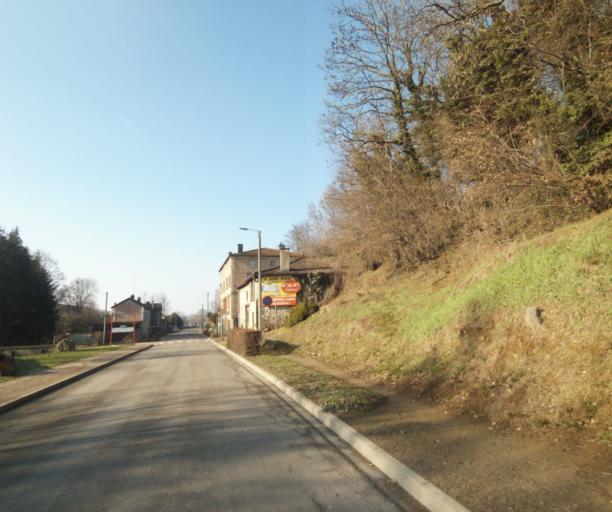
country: FR
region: Champagne-Ardenne
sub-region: Departement de la Haute-Marne
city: Wassy
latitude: 48.4936
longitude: 4.9606
